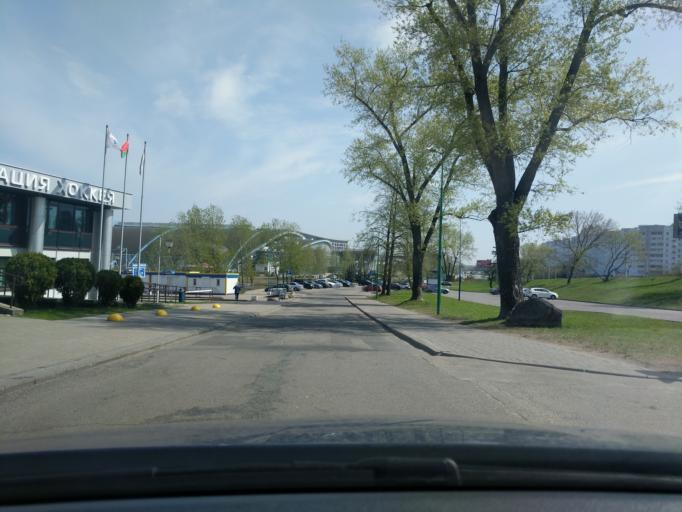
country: BY
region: Minsk
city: Minsk
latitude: 53.9341
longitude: 27.5042
